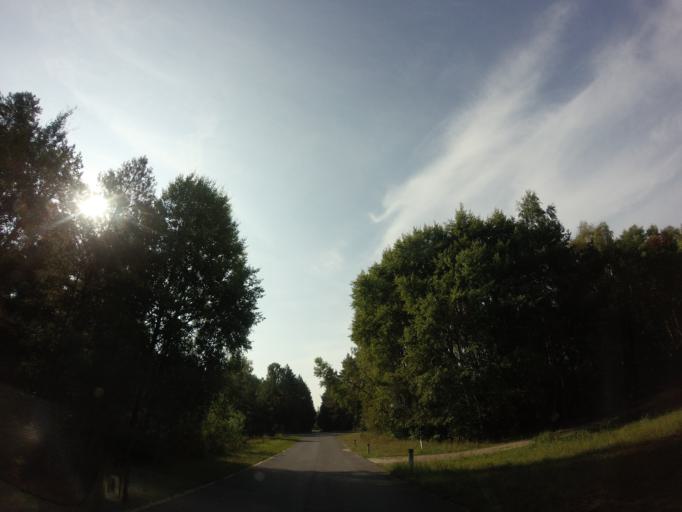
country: PL
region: West Pomeranian Voivodeship
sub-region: Powiat drawski
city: Drawsko Pomorskie
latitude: 53.4727
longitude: 15.7303
